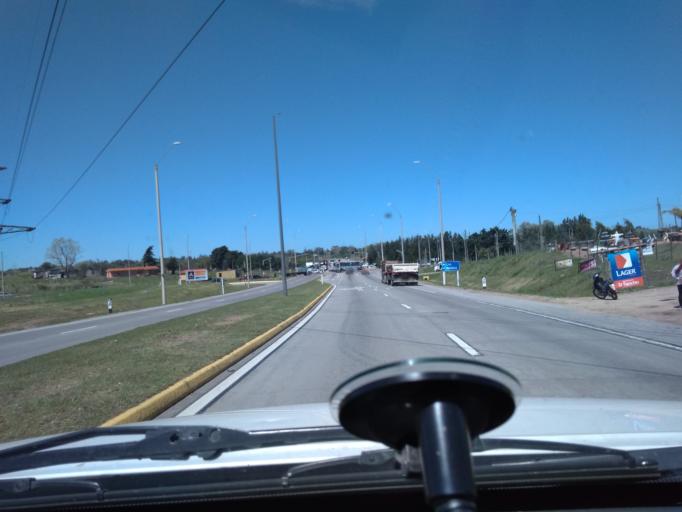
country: UY
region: Canelones
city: La Paz
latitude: -34.7944
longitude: -56.1666
